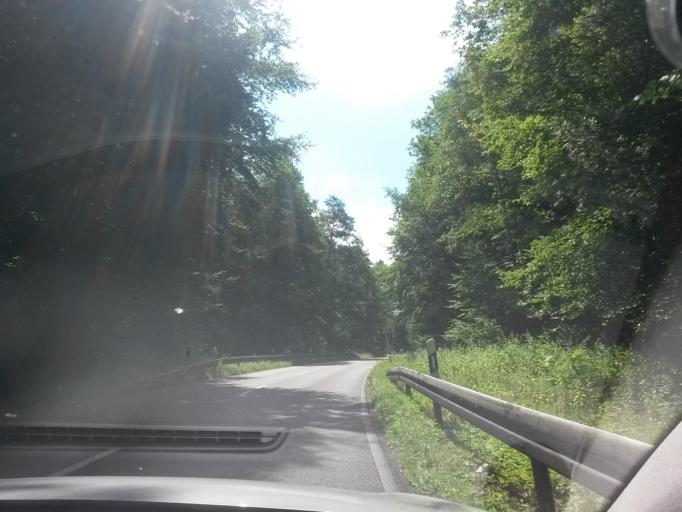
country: DE
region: Baden-Wuerttemberg
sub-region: Karlsruhe Region
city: Ettlingen
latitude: 48.9130
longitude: 8.4024
